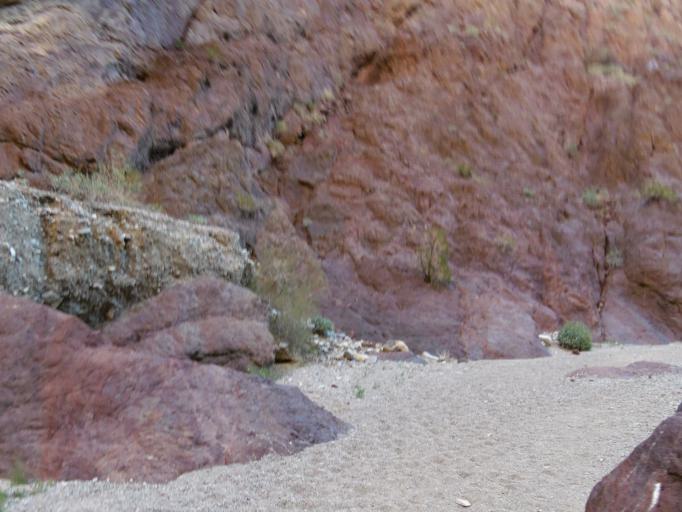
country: US
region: Nevada
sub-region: Clark County
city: Boulder City
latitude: 35.9725
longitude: -114.7166
